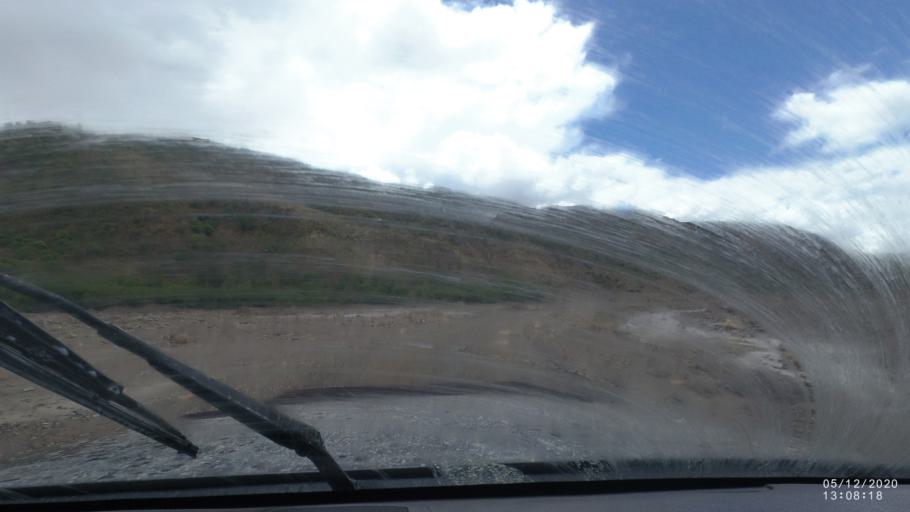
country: BO
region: Cochabamba
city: Sipe Sipe
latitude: -17.5616
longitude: -66.4517
